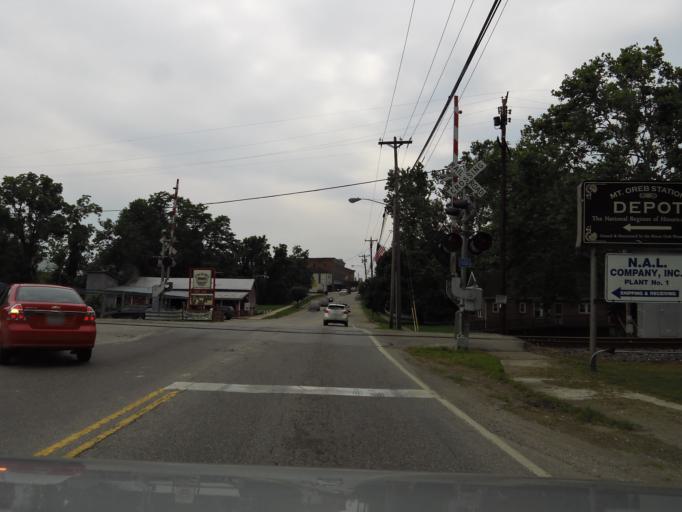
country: US
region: Ohio
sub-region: Brown County
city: Mount Orab
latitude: 39.0298
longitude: -83.9193
